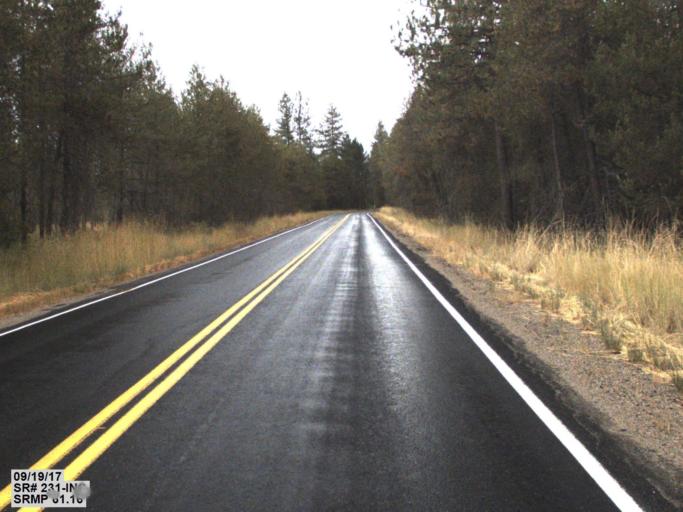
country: US
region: Washington
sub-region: Stevens County
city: Chewelah
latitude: 48.0430
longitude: -117.7392
